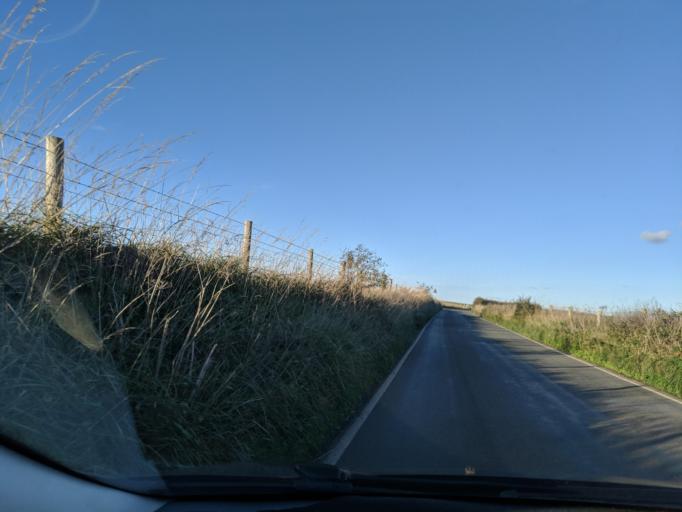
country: GB
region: England
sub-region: Plymouth
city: Plymstock
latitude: 50.3345
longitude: -4.1031
